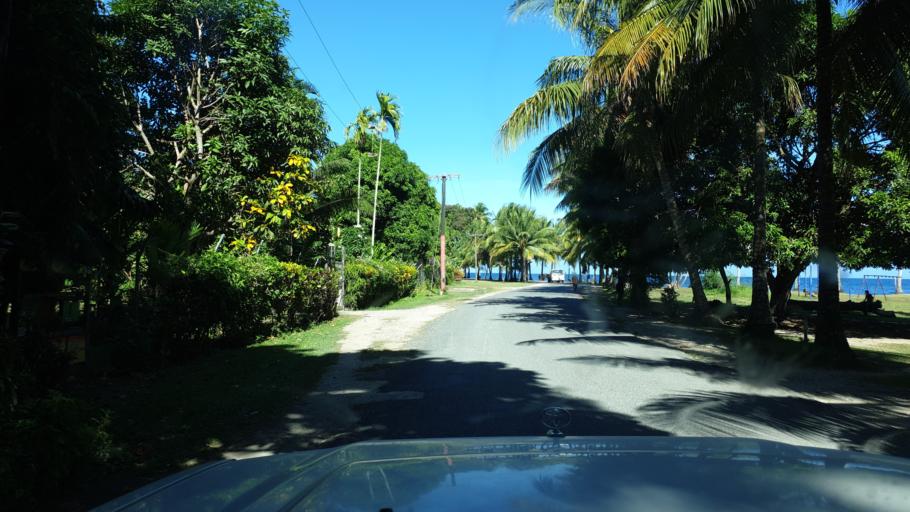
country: PG
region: Madang
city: Madang
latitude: -5.2271
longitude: 145.8017
